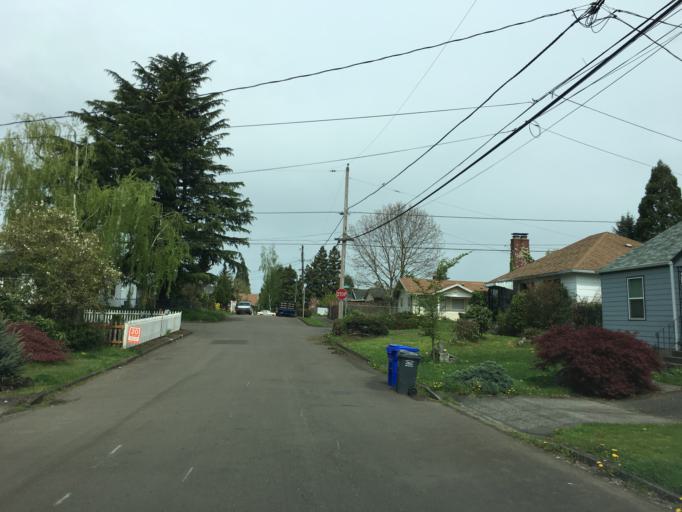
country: US
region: Oregon
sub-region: Multnomah County
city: Lents
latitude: 45.5562
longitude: -122.5747
